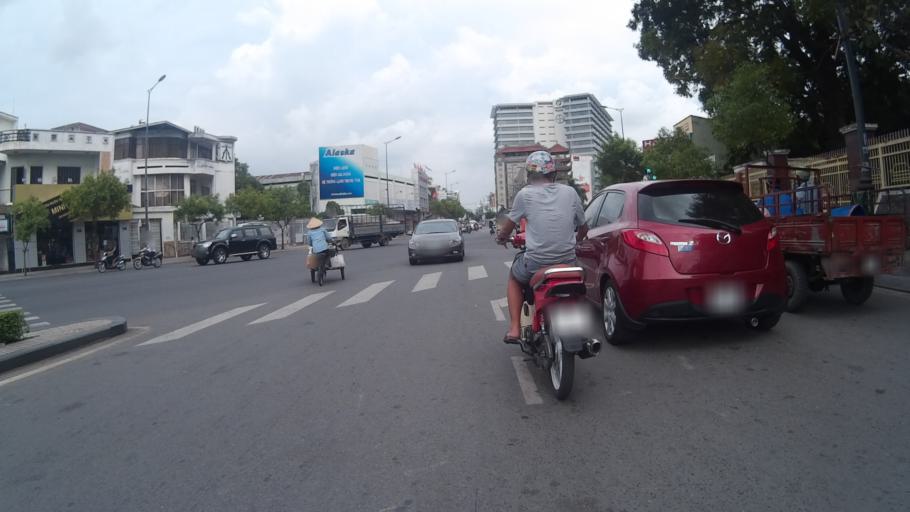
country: VN
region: Ho Chi Minh City
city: Quan Phu Nhuan
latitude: 10.7980
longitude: 106.6711
